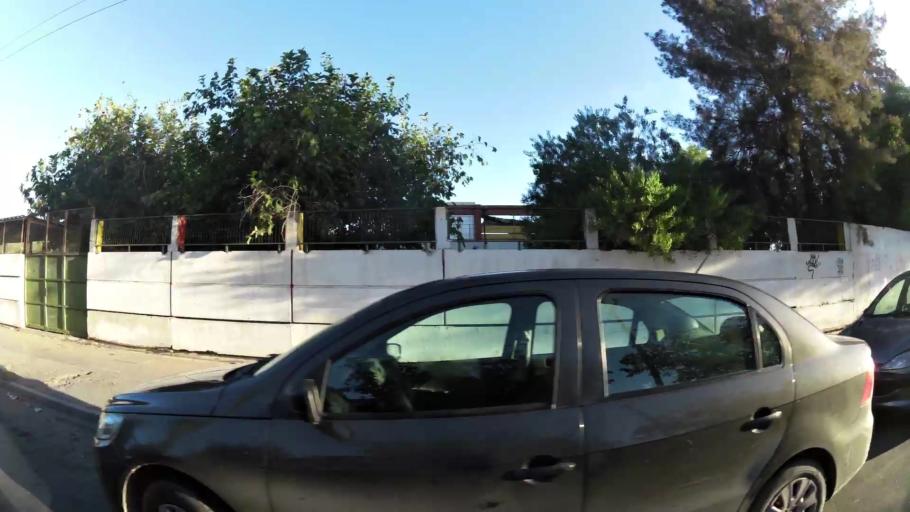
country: AR
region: San Juan
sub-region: Departamento de Santa Lucia
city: Santa Lucia
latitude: -31.5404
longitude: -68.5110
